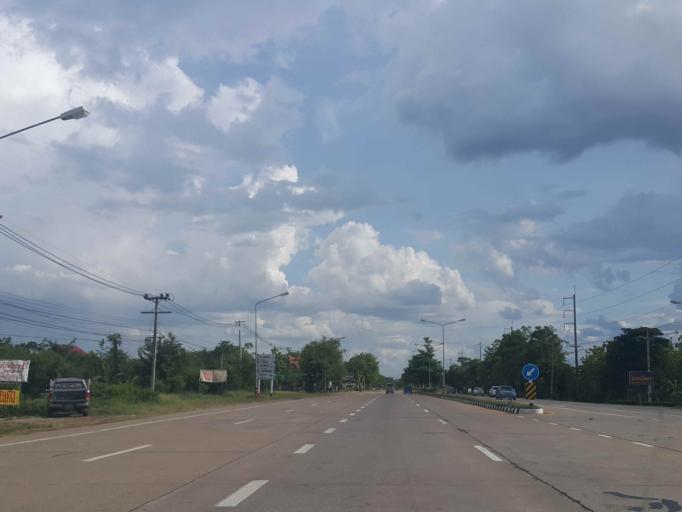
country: TH
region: Phrae
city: Sung Men
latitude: 18.0229
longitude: 100.1103
